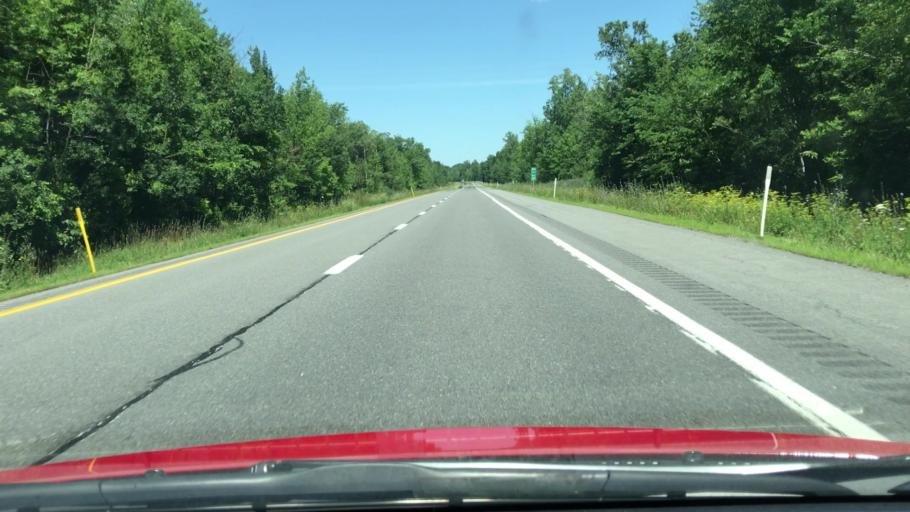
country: US
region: New York
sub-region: Clinton County
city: Champlain
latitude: 44.9083
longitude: -73.4509
